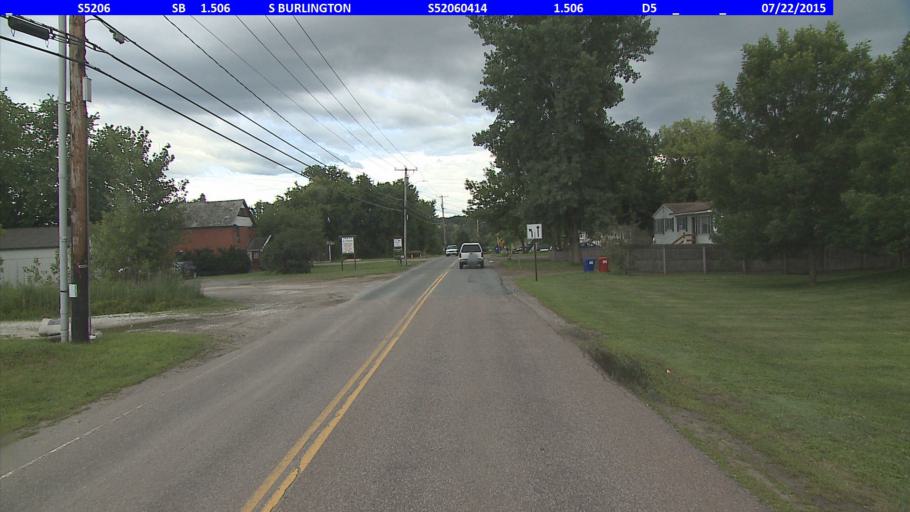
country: US
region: Vermont
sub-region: Chittenden County
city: South Burlington
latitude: 44.4870
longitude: -73.1620
